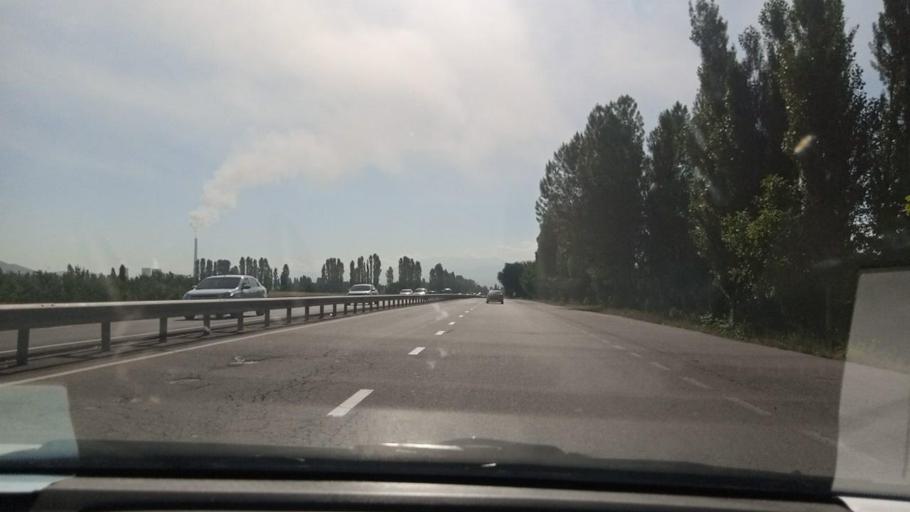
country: UZ
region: Toshkent
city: Ohangaron
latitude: 40.9095
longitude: 69.7550
